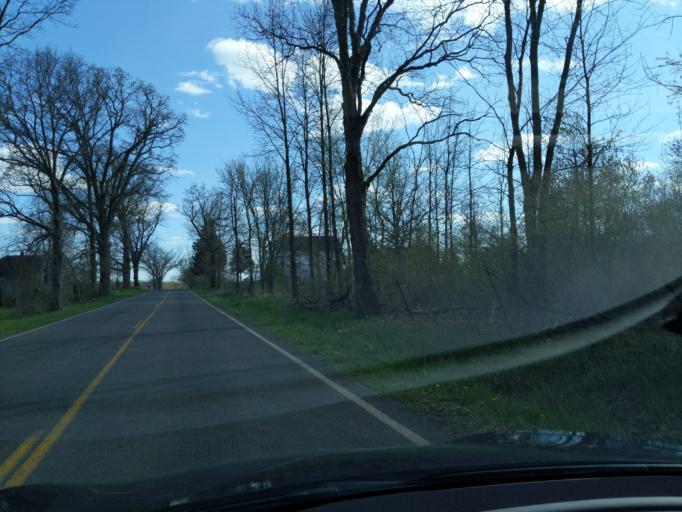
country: US
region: Michigan
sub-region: Ingham County
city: Leslie
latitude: 42.3830
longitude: -84.5416
